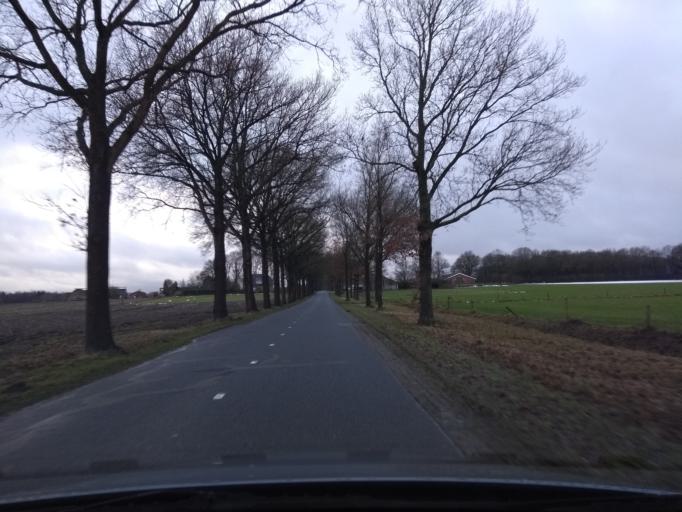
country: NL
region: Overijssel
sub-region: Gemeente Twenterand
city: Den Ham
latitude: 52.3935
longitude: 6.5167
